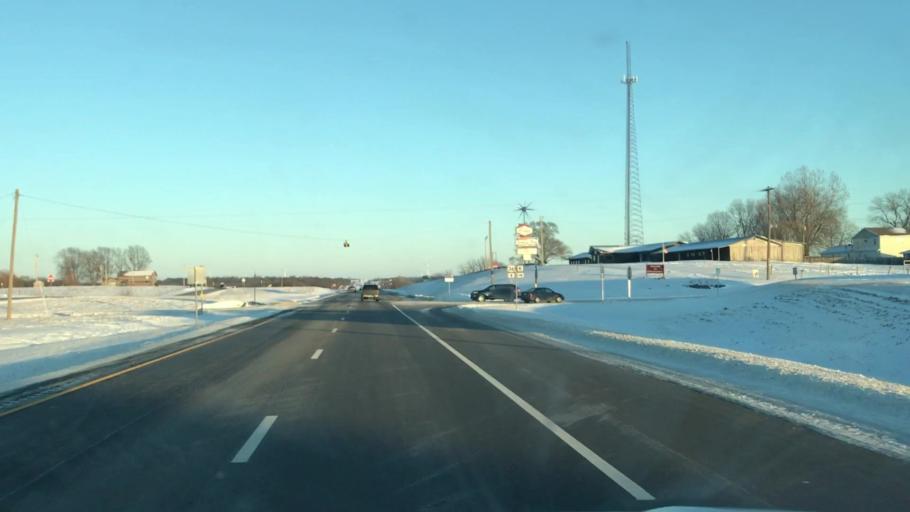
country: US
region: Missouri
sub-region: Clinton County
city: Gower
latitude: 39.7620
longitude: -94.4984
